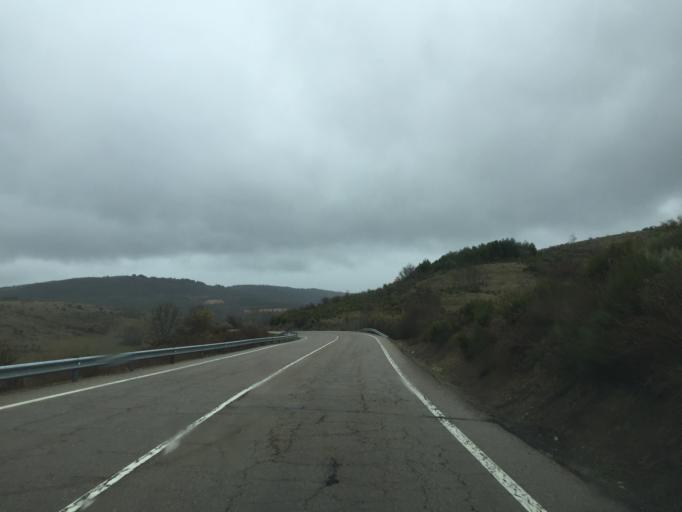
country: ES
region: Castille and Leon
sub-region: Provincia de Leon
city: Carrocera
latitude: 42.7846
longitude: -5.7480
